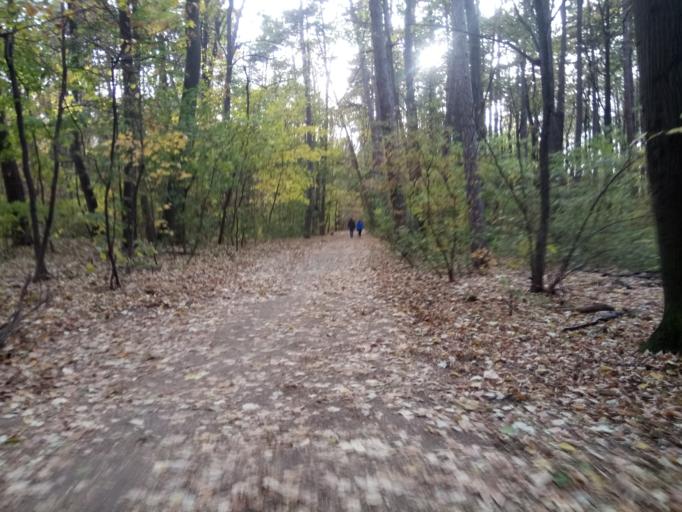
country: BG
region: Sofia-Capital
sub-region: Stolichna Obshtina
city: Sofia
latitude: 42.6808
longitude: 23.3469
